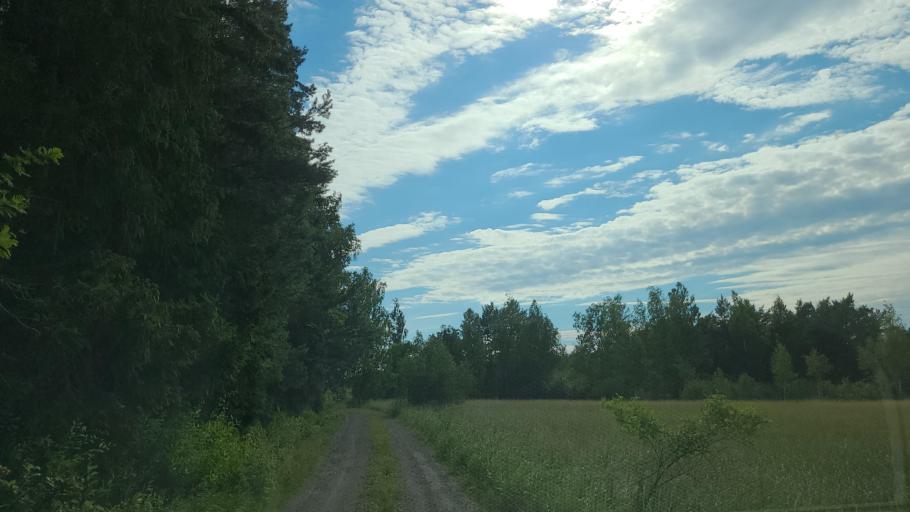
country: FI
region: Varsinais-Suomi
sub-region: Turku
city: Rymaettylae
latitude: 60.2909
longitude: 21.9681
